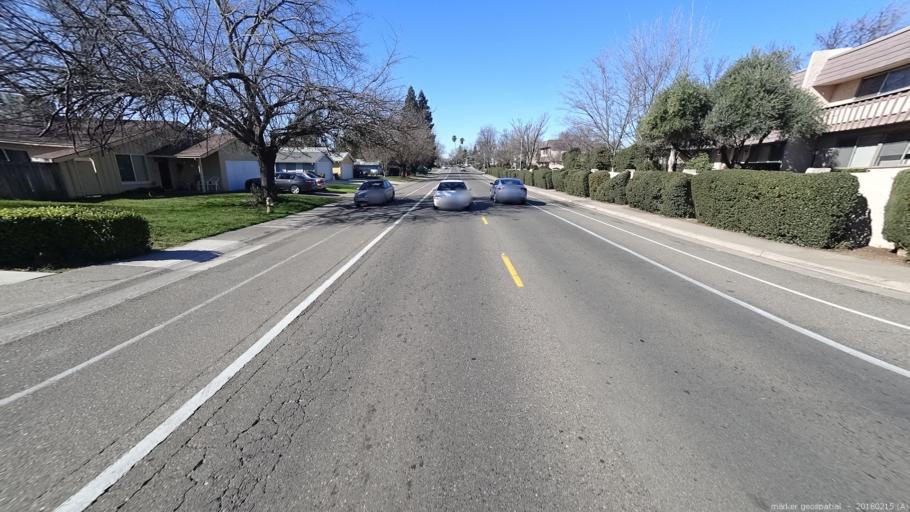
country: US
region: California
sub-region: Sacramento County
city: Foothill Farms
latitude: 38.6680
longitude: -121.3245
